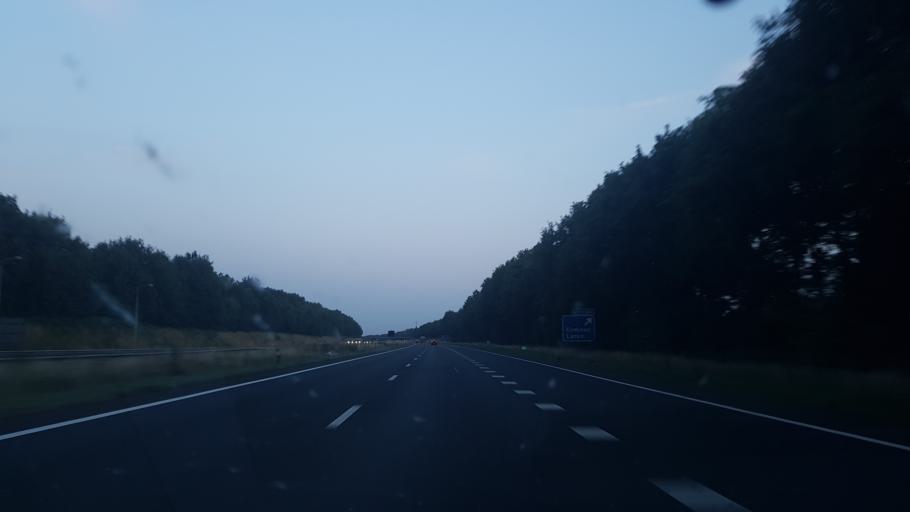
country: NL
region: North Holland
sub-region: Gemeente Blaricum
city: Blaricum
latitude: 52.2610
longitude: 5.2521
